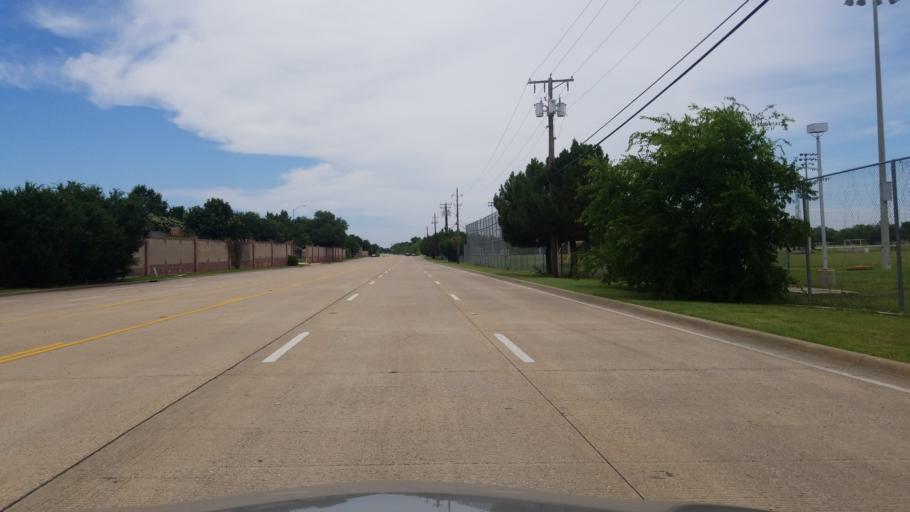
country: US
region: Texas
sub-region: Dallas County
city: Grand Prairie
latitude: 32.6838
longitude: -96.9850
